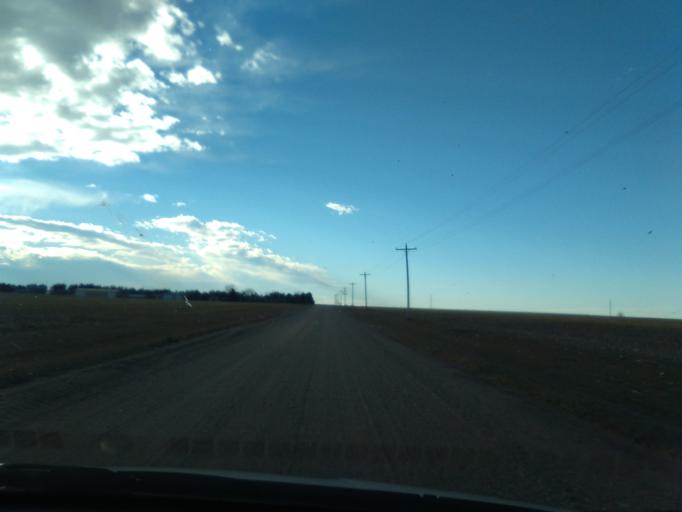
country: US
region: Nebraska
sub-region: Kearney County
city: Minden
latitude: 40.3649
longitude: -98.8580
